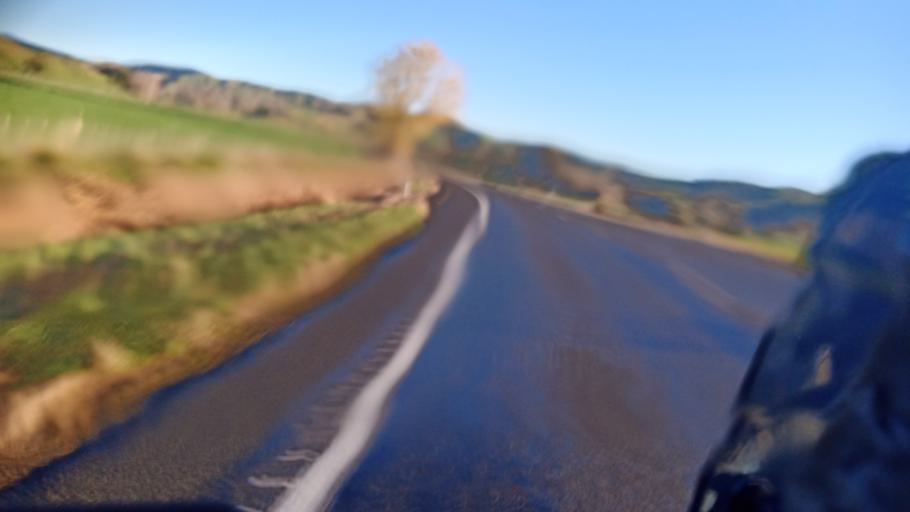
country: NZ
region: Hawke's Bay
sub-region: Wairoa District
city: Wairoa
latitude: -39.0204
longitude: 177.3742
